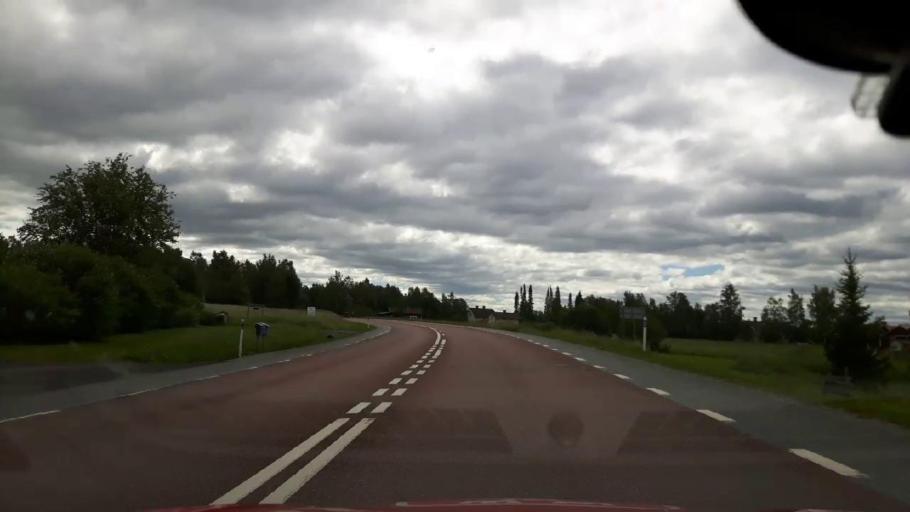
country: SE
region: Jaemtland
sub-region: Braecke Kommun
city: Braecke
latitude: 62.8281
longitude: 15.3179
